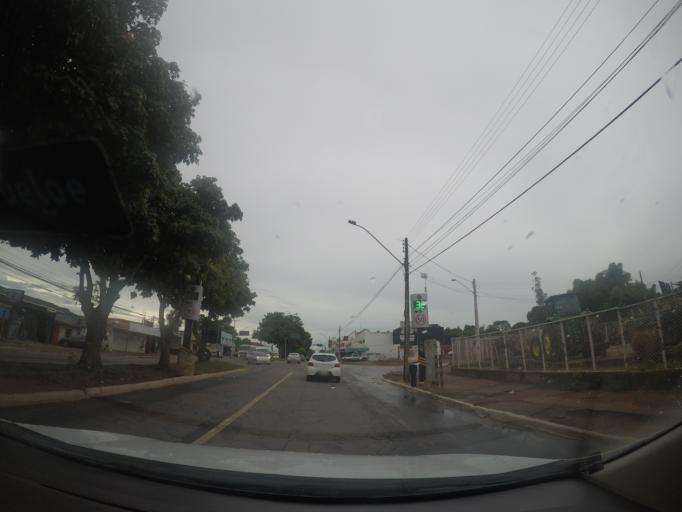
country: BR
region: Goias
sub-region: Goiania
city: Goiania
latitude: -16.6352
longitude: -49.2374
